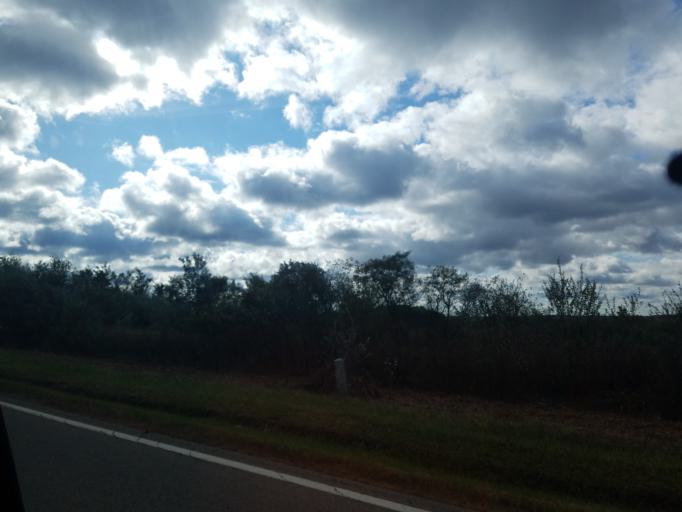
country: US
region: Ohio
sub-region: Vinton County
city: McArthur
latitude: 39.1773
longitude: -82.4513
